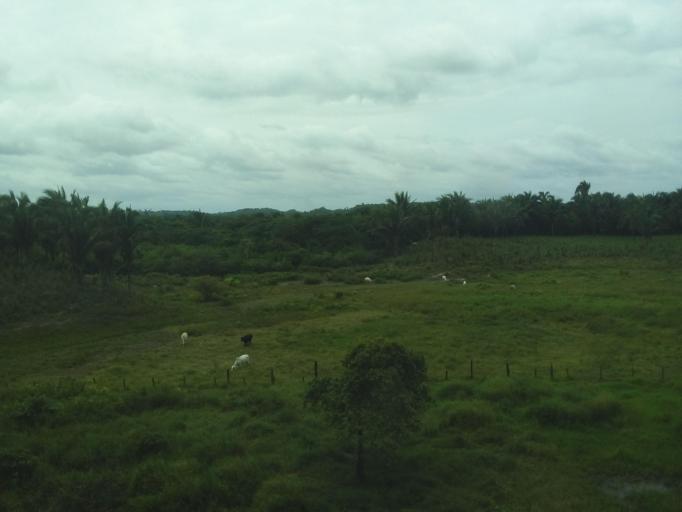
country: BR
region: Maranhao
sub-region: Santa Ines
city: Santa Ines
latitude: -3.7071
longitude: -45.9353
